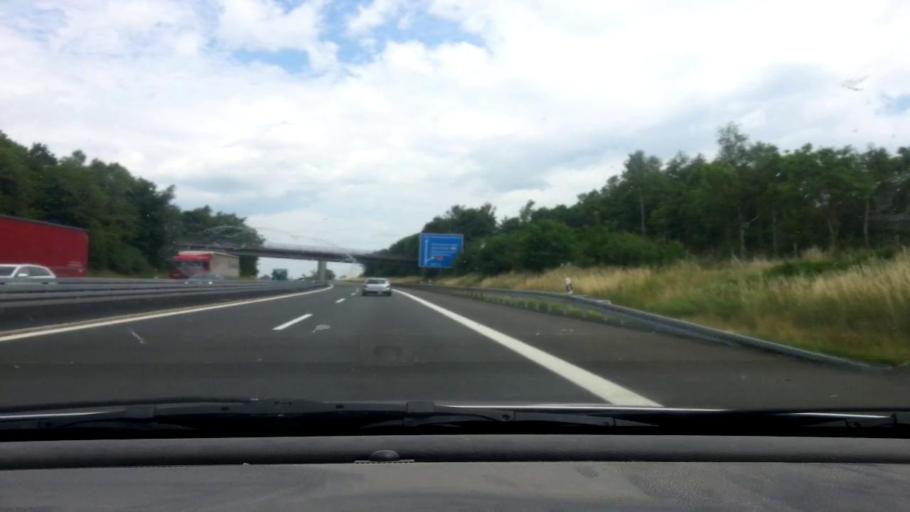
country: DE
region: Bavaria
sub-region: Upper Palatinate
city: Mitterteich
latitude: 49.9257
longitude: 12.2255
